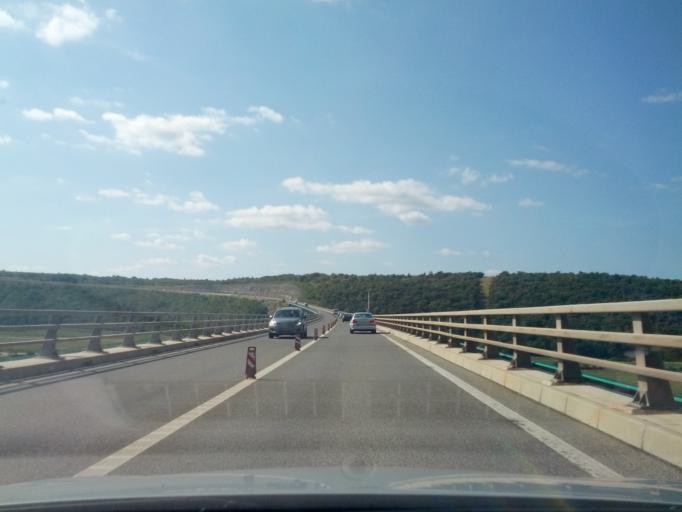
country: HR
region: Istarska
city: Novigrad
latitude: 45.3338
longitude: 13.6252
